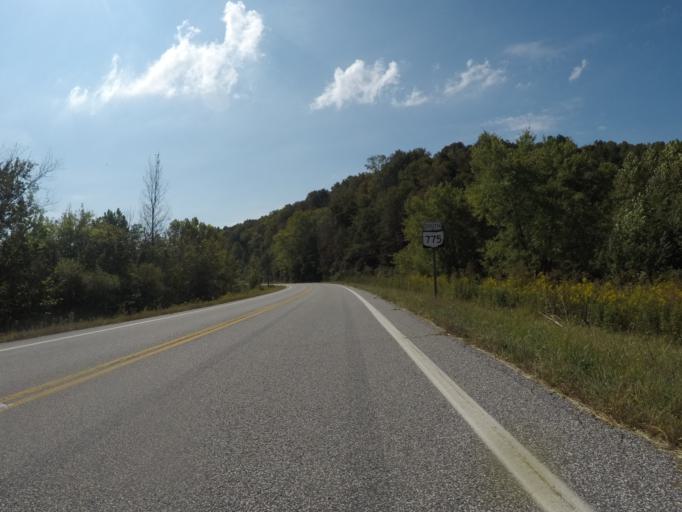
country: US
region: West Virginia
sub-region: Cabell County
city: Lesage
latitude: 38.5465
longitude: -82.3934
